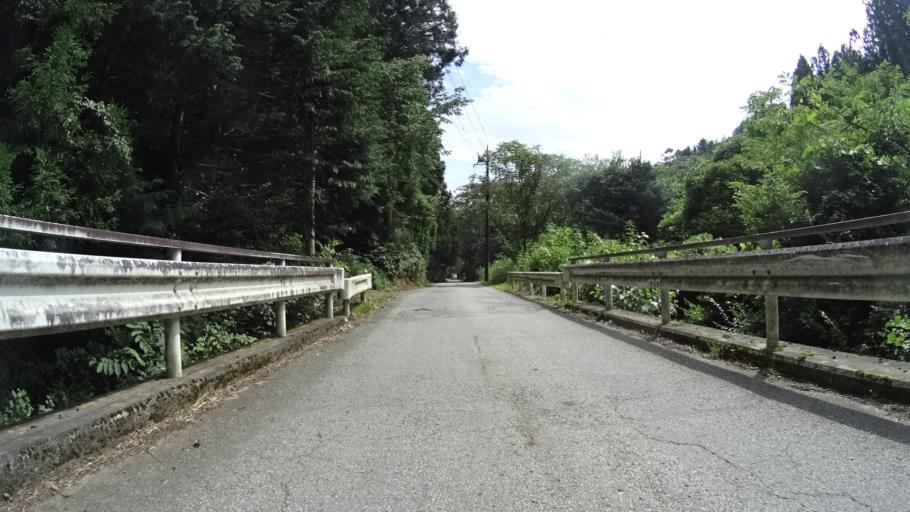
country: JP
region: Yamanashi
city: Nirasaki
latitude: 35.7820
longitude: 138.5346
